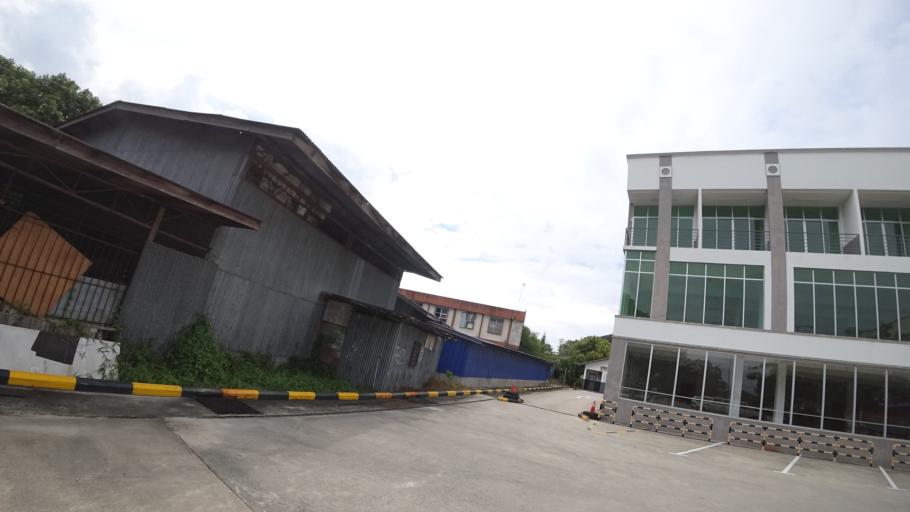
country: BN
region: Tutong
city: Tutong
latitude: 4.8029
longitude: 114.6535
